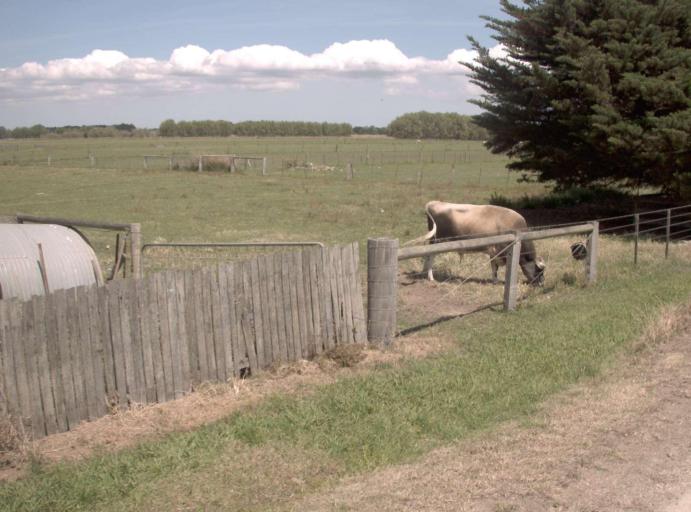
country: AU
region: Victoria
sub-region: Wellington
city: Heyfield
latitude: -38.0458
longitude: 146.8761
